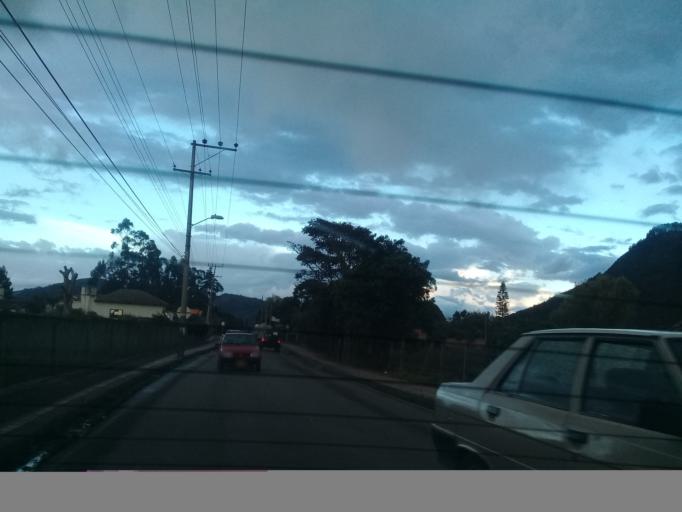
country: CO
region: Cundinamarca
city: Tabio
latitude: 4.9211
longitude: -74.0880
